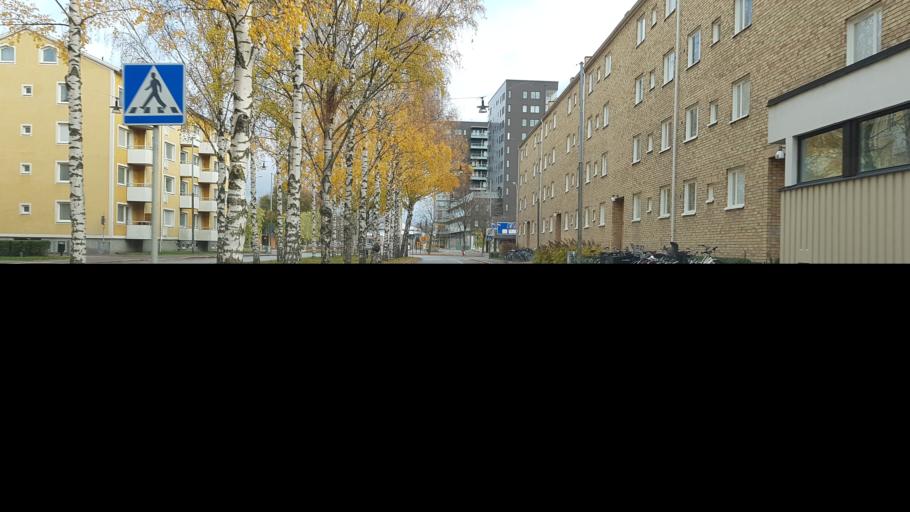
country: SE
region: Uppsala
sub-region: Uppsala Kommun
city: Uppsala
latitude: 59.8658
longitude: 17.6463
